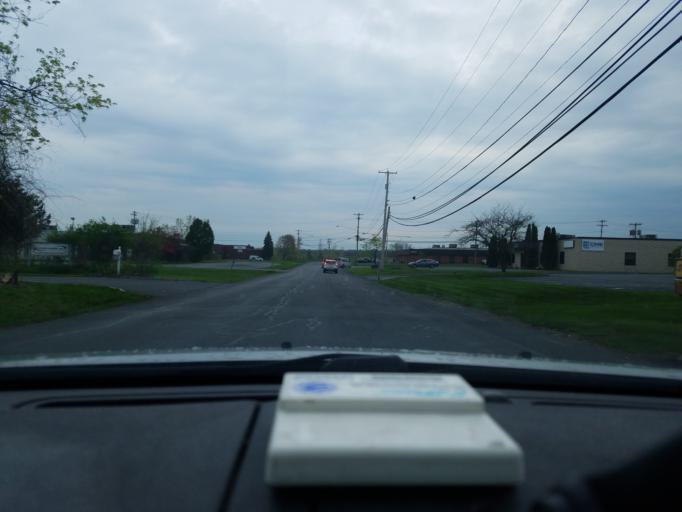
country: US
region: New York
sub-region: Onondaga County
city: East Syracuse
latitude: 43.1013
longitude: -76.0879
